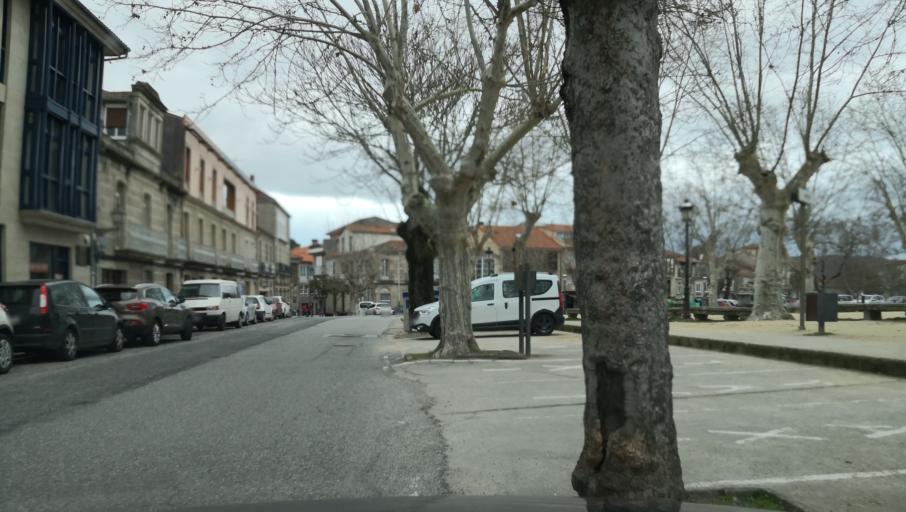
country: ES
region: Galicia
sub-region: Provincia de Ourense
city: Allariz
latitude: 42.1885
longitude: -7.7994
